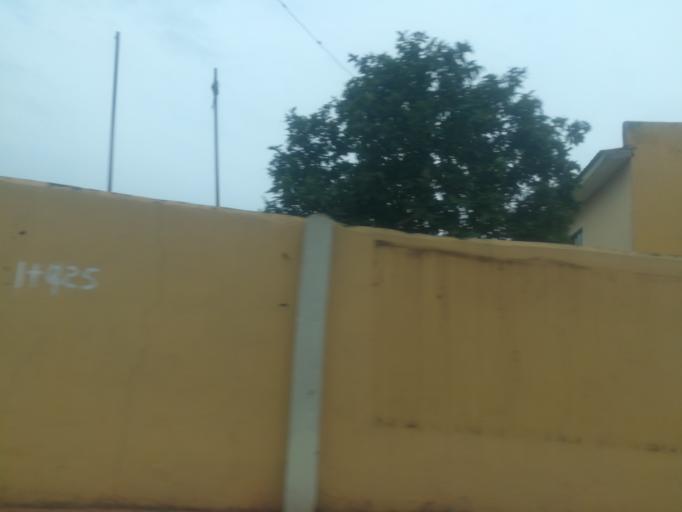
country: NG
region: Oyo
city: Egbeda
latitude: 7.4062
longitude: 3.9792
